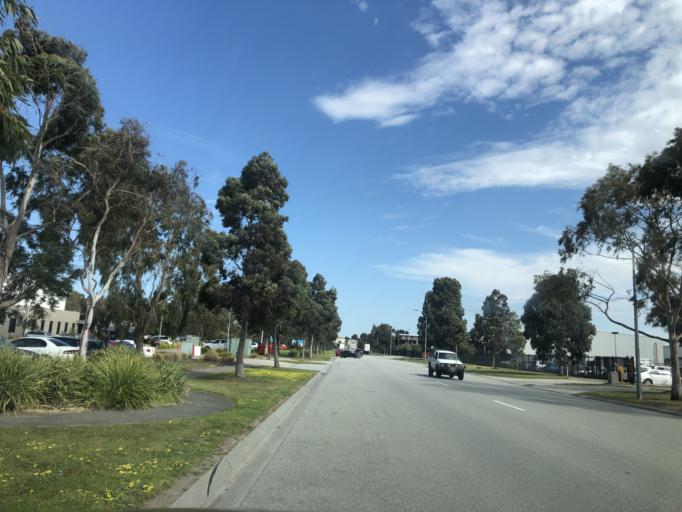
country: AU
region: Victoria
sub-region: Casey
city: Hampton Park
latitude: -38.0363
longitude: 145.2344
